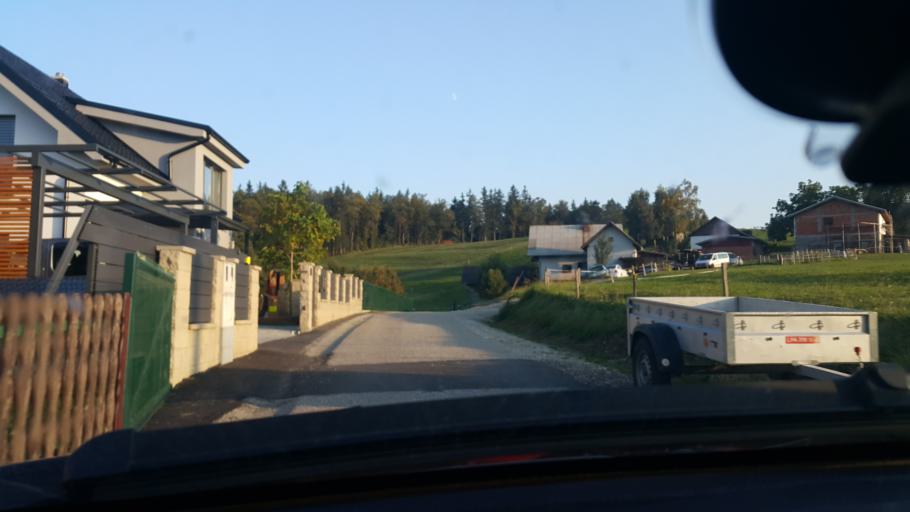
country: SI
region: Race-Fram
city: Morje
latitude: 46.4554
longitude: 15.6018
